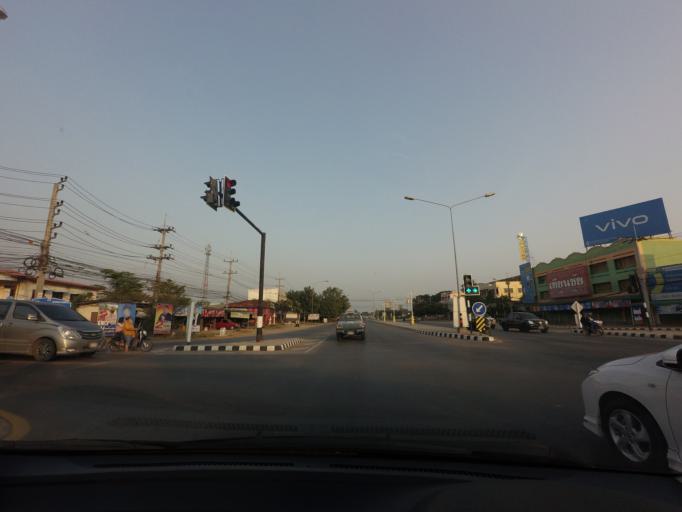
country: TH
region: Sukhothai
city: Sukhothai
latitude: 17.0212
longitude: 99.8215
